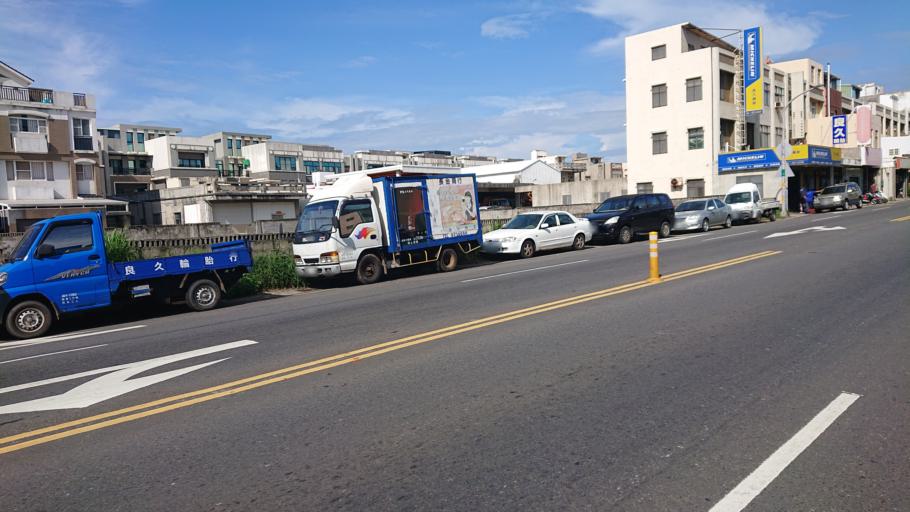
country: TW
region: Taiwan
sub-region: Penghu
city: Ma-kung
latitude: 23.5632
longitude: 119.5906
